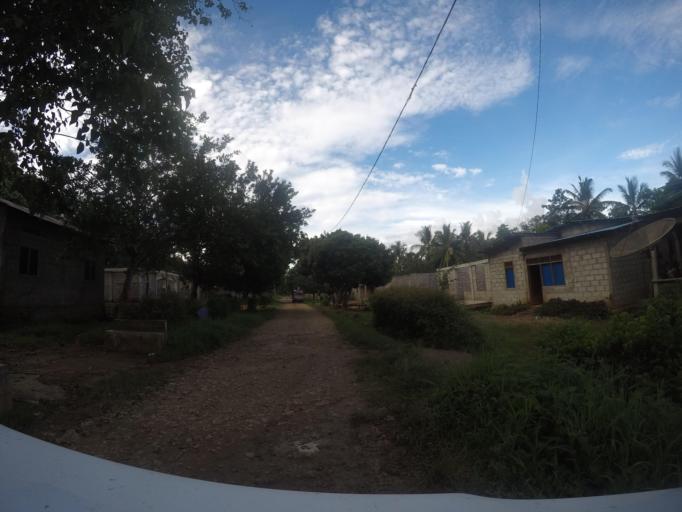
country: TL
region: Lautem
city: Lospalos
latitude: -8.4998
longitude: 126.9960
